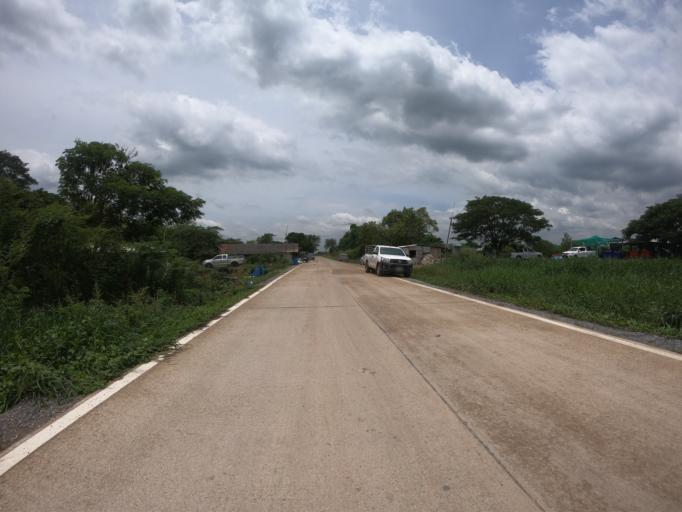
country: TH
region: Pathum Thani
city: Ban Lam Luk Ka
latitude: 13.9817
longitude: 100.8532
